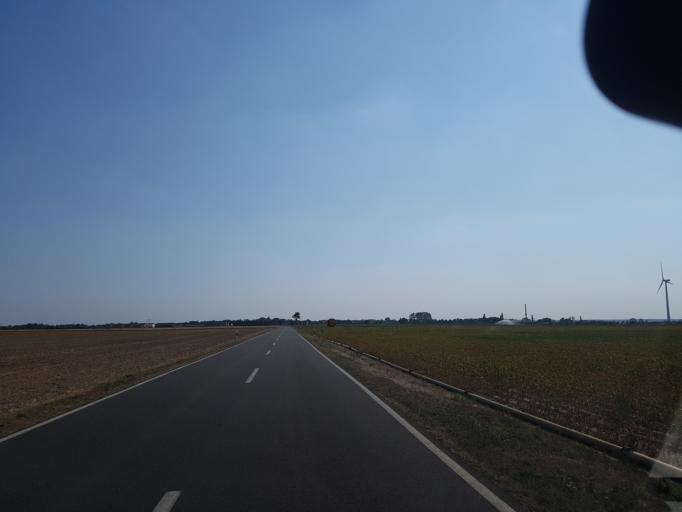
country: DE
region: Saxony-Anhalt
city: Prettin
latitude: 51.6592
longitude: 12.9888
